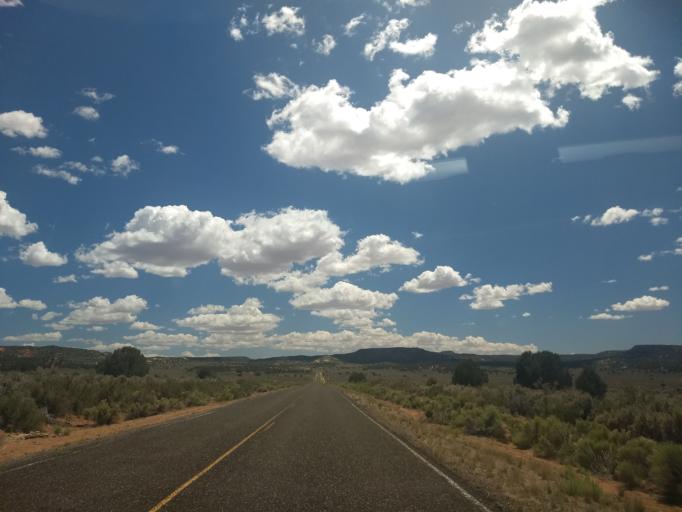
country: US
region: Utah
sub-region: Kane County
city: Kanab
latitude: 37.1677
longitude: -112.6636
